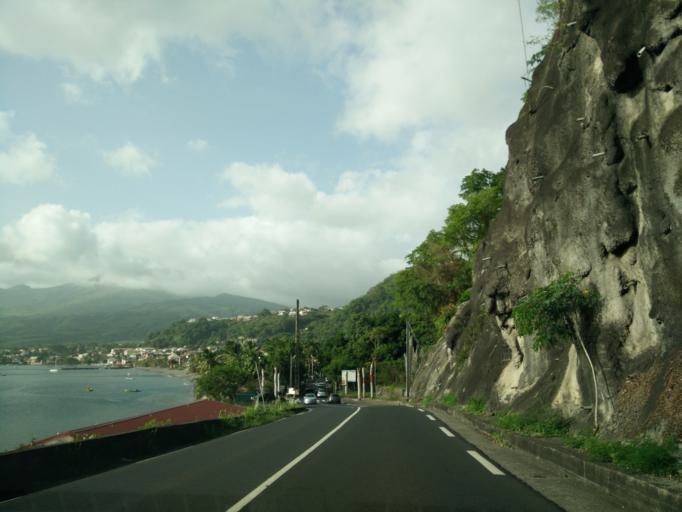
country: MQ
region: Martinique
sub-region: Martinique
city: Saint-Pierre
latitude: 14.7351
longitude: -61.1775
